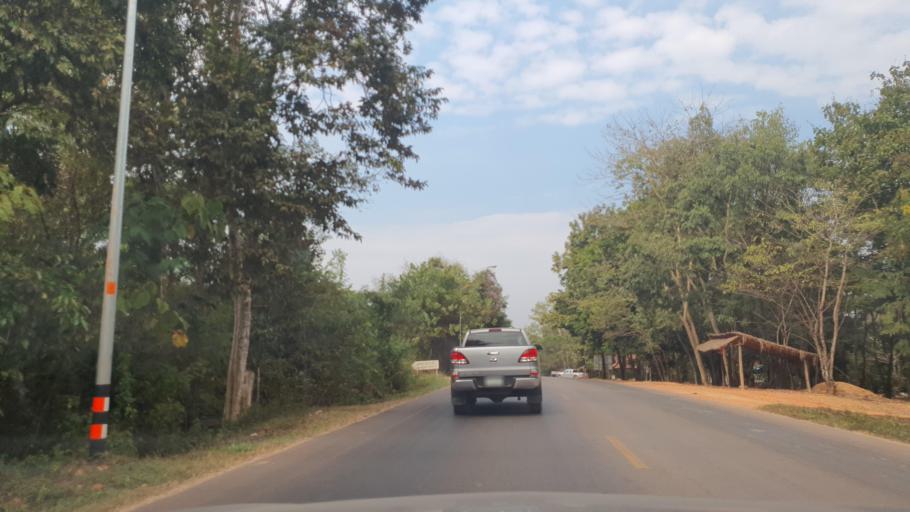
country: TH
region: Changwat Bueng Kan
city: Si Wilai
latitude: 18.2799
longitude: 103.8295
